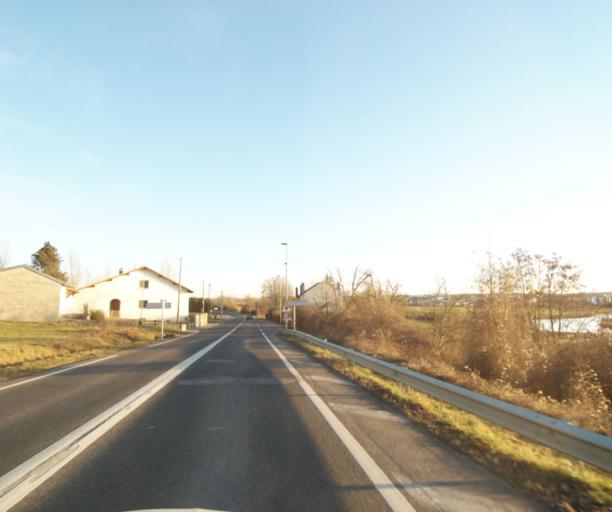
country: FR
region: Lorraine
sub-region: Departement de Meurthe-et-Moselle
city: Laneuveville-devant-Nancy
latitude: 48.6688
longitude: 6.2328
